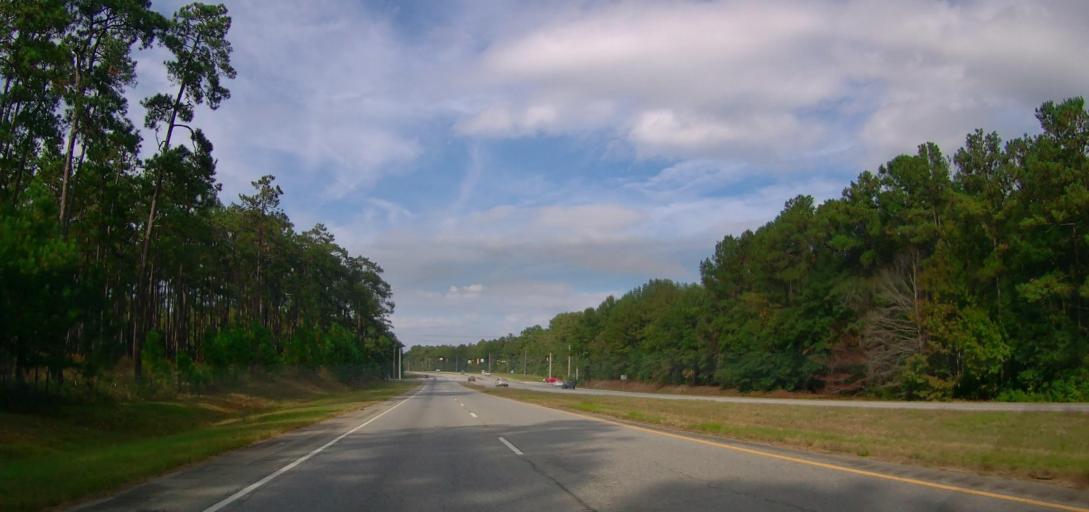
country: US
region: Georgia
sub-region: Thomas County
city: Thomasville
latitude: 30.8498
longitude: -84.0069
